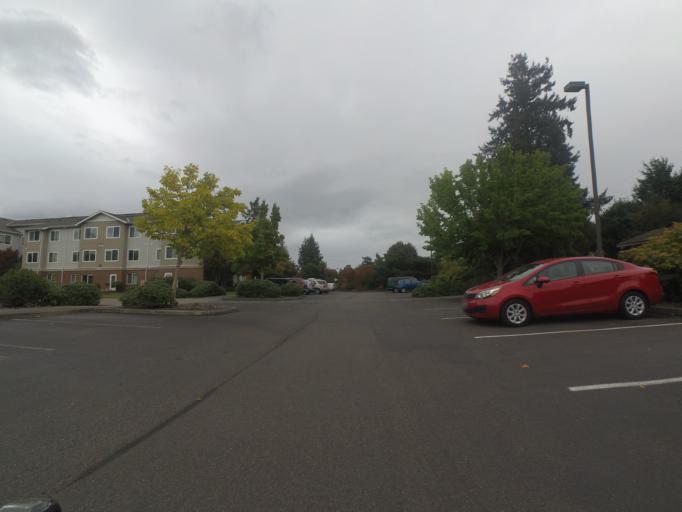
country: US
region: Washington
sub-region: Pierce County
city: Lakewood
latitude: 47.1545
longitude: -122.5072
